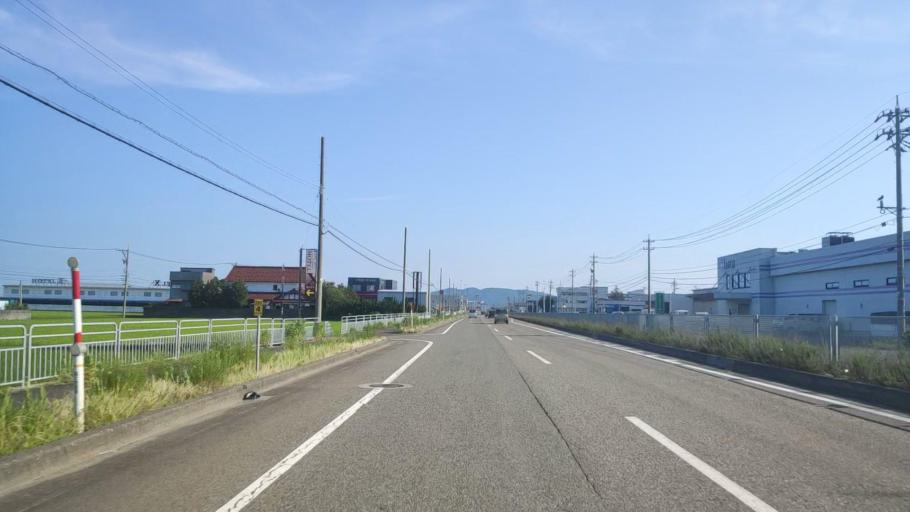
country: JP
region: Fukui
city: Maruoka
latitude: 36.1620
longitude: 136.2638
